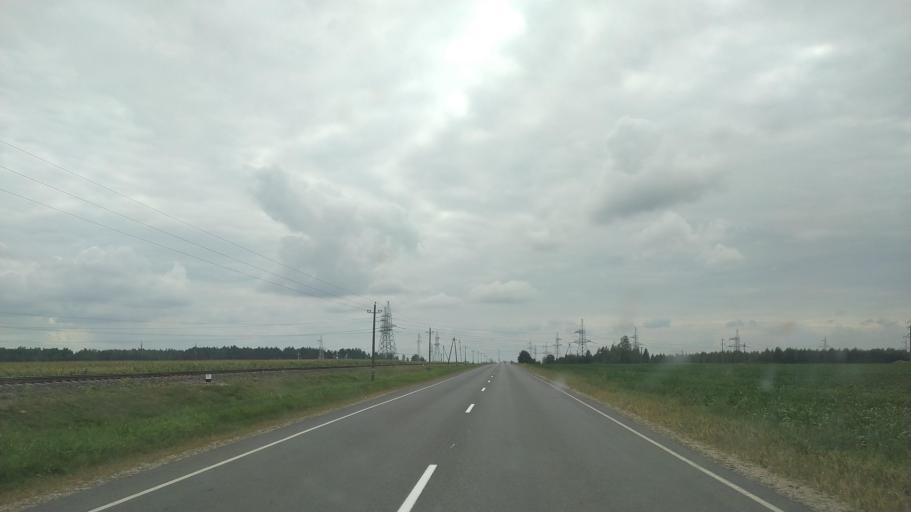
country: BY
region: Brest
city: Byelaazyorsk
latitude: 52.5190
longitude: 25.1516
